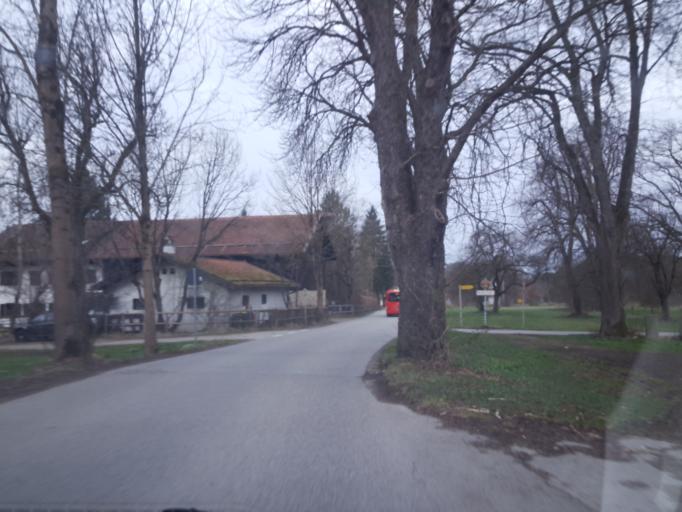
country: DE
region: Bavaria
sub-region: Upper Bavaria
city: Bad Heilbrunn
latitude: 47.7413
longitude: 11.4384
